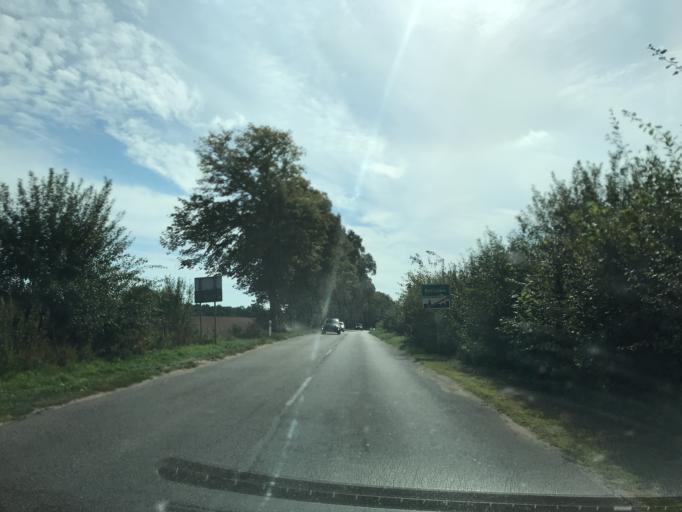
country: PL
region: Pomeranian Voivodeship
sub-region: Powiat pucki
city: Krokowa
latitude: 54.7742
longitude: 18.1613
